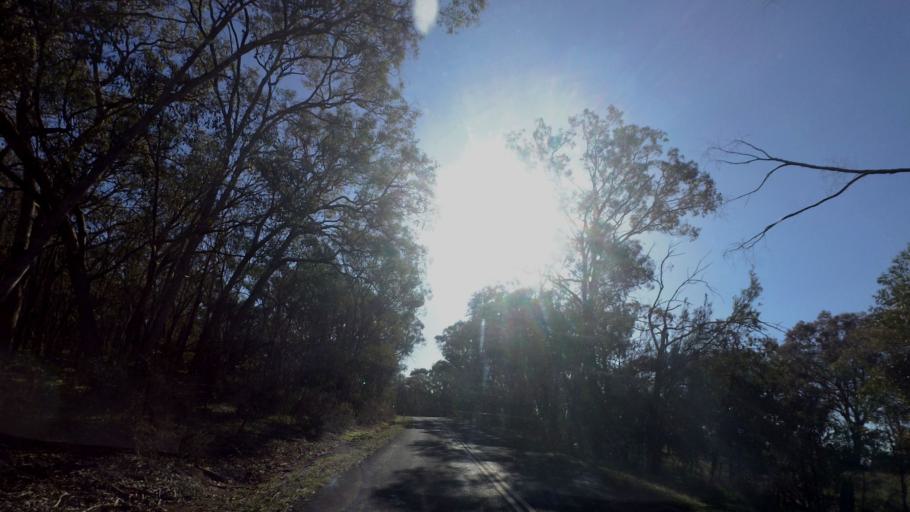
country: AU
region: Victoria
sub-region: Greater Bendigo
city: Kangaroo Flat
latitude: -36.8861
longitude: 144.2864
